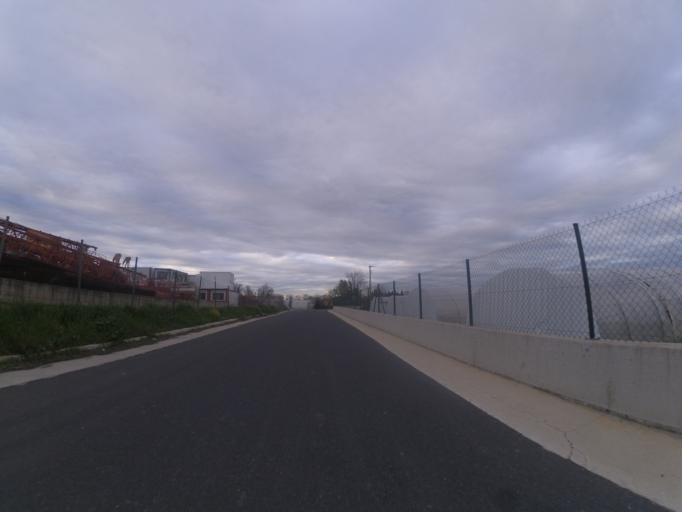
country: FR
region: Languedoc-Roussillon
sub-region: Departement des Pyrenees-Orientales
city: Saint-Esteve
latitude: 42.7015
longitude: 2.8682
